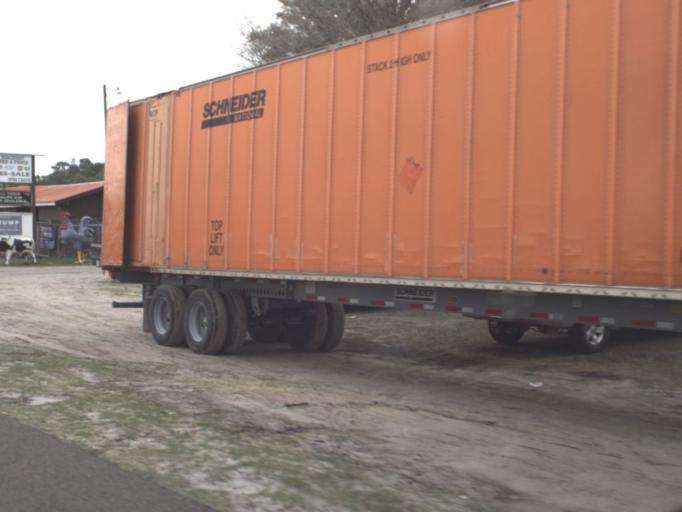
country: US
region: Florida
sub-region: Lake County
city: Umatilla
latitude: 28.9787
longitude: -81.6452
